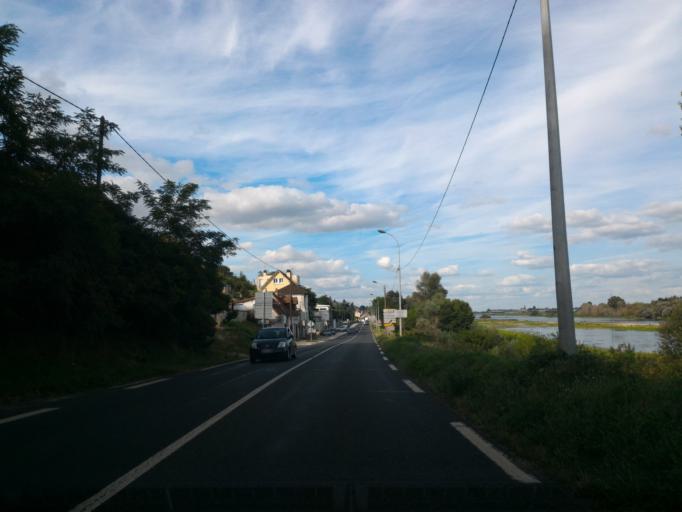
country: FR
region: Centre
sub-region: Departement du Loir-et-Cher
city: Chailles
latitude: 47.5686
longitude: 1.3061
